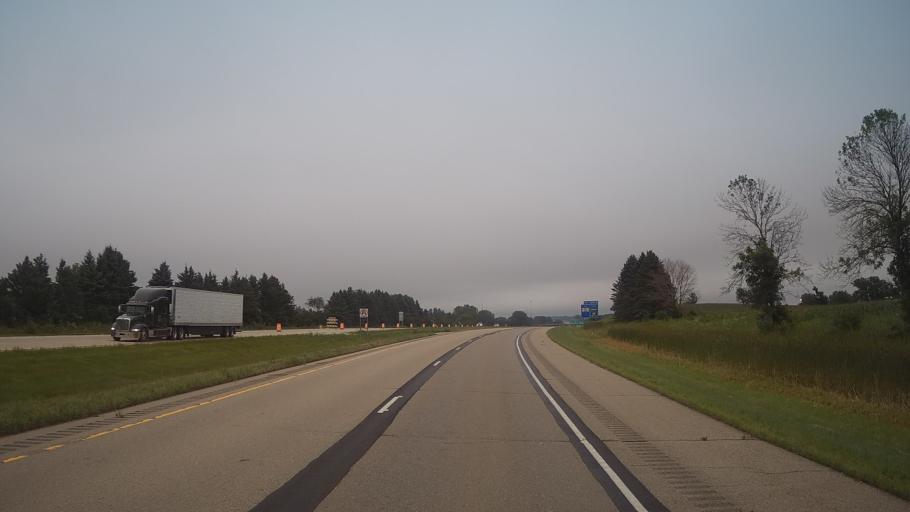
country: US
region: Minnesota
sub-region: Olmsted County
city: Stewartville
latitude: 43.8803
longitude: -92.5027
